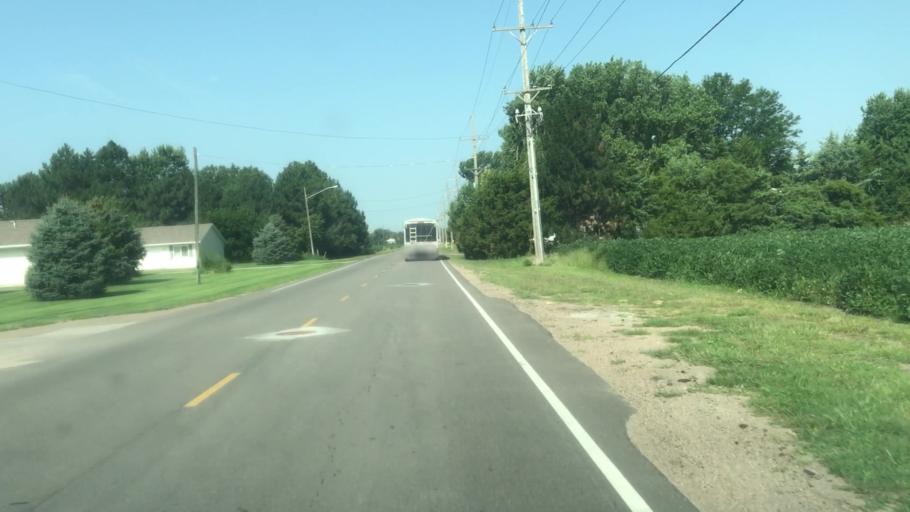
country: US
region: Nebraska
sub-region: Hall County
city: Grand Island
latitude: 40.9455
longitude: -98.3242
